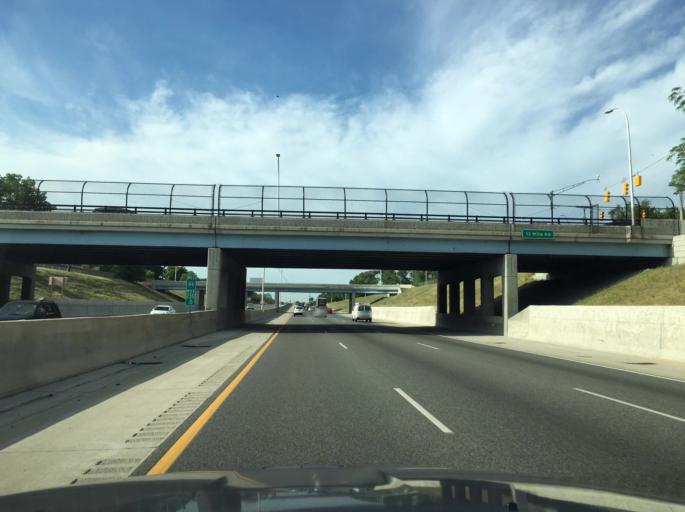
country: US
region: Michigan
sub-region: Macomb County
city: Roseville
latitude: 42.5107
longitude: -82.9184
